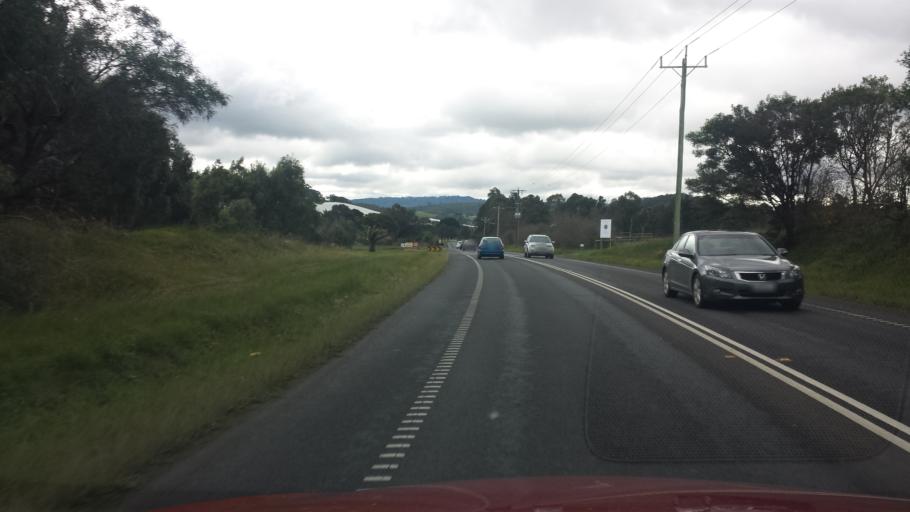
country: AU
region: Victoria
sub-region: Casey
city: Narre Warren North
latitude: -37.9760
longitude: 145.3150
